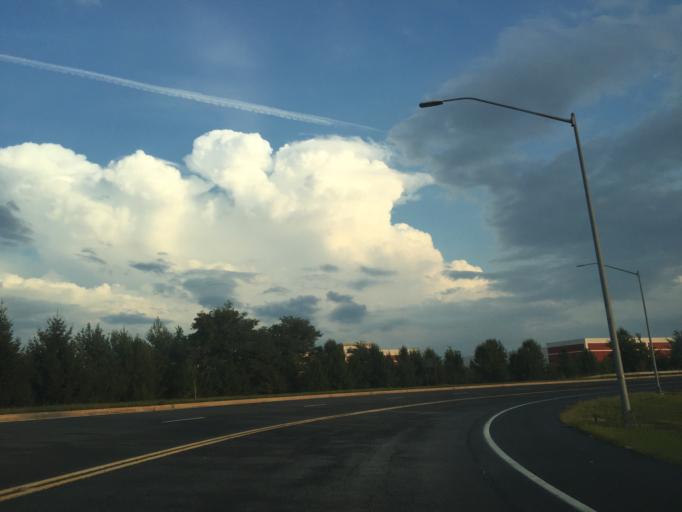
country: US
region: Maryland
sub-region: Harford County
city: Riverside
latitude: 39.4709
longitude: -76.2320
